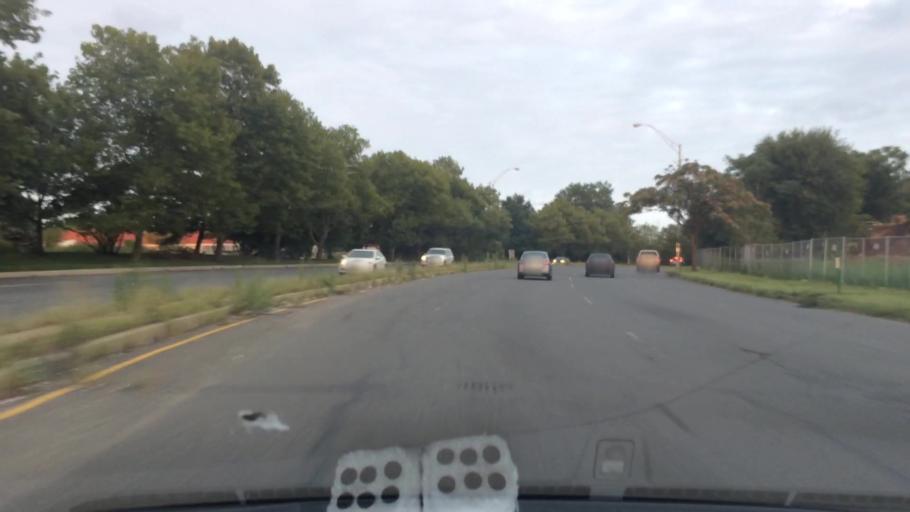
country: US
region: Pennsylvania
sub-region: Delaware County
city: Colwyn
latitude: 39.8955
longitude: -75.2328
